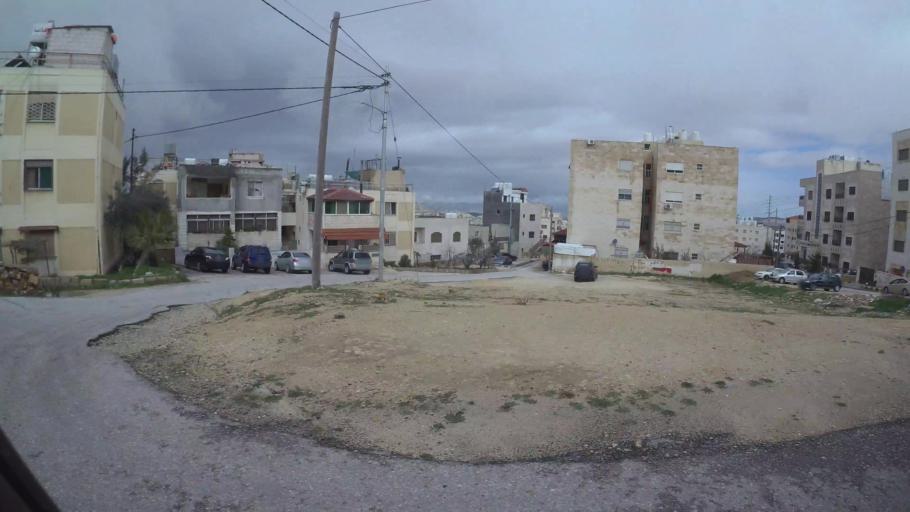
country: JO
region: Amman
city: Al Jubayhah
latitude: 32.0581
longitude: 35.8880
